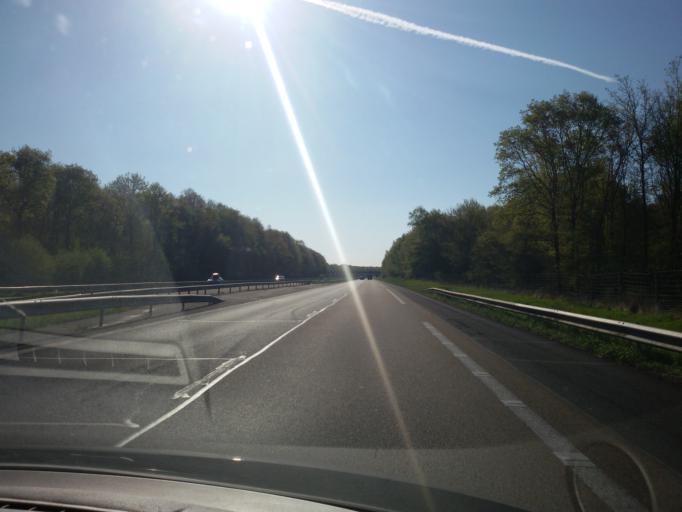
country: FR
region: Bourgogne
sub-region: Departement de l'Yonne
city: Cheroy
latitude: 48.1124
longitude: 2.9958
